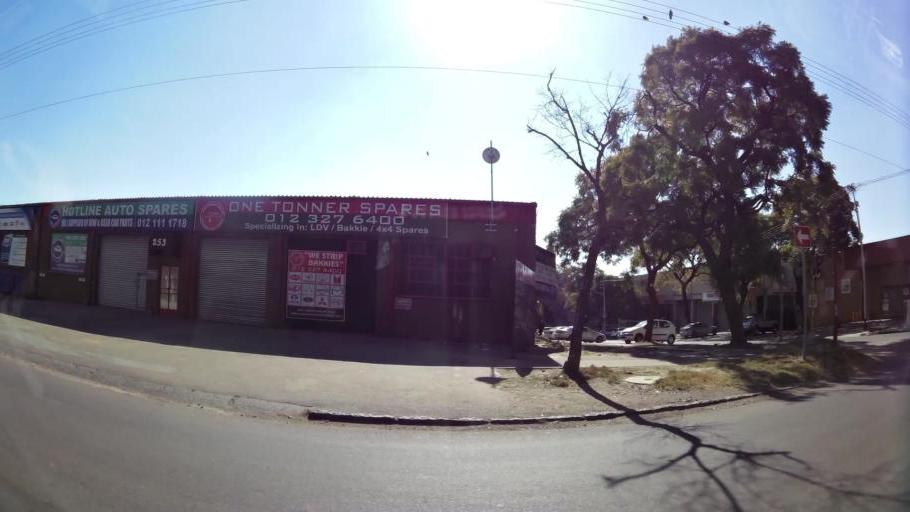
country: ZA
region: Gauteng
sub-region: City of Tshwane Metropolitan Municipality
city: Pretoria
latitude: -25.7544
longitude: 28.1652
